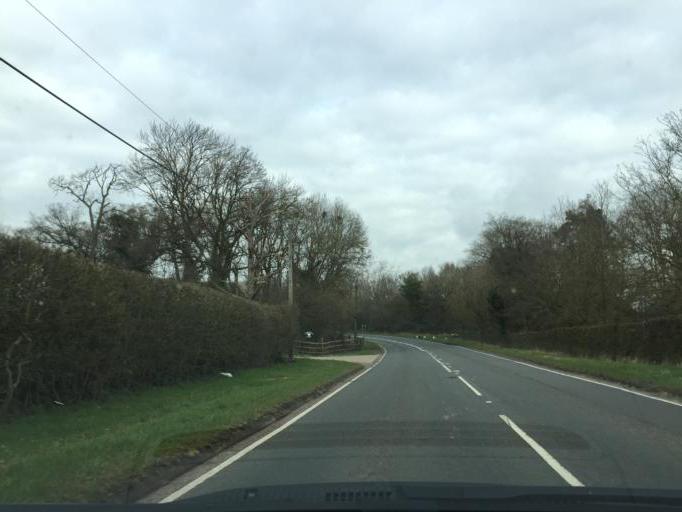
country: GB
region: England
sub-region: Warwickshire
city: Henley in Arden
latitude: 52.2965
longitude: -1.8277
